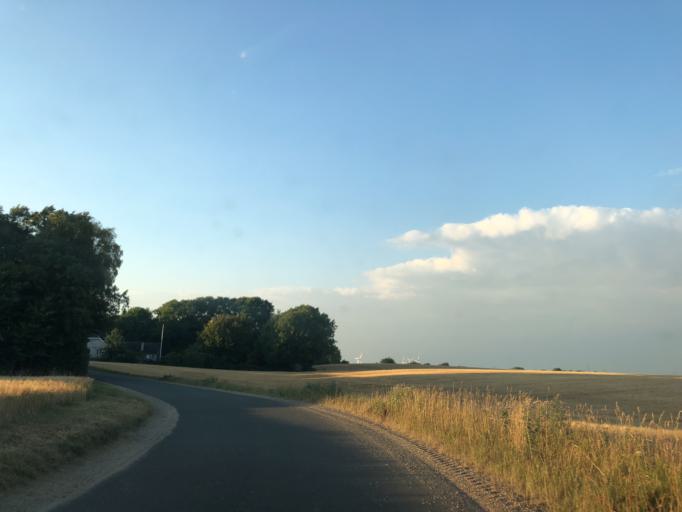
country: DK
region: Central Jutland
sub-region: Holstebro Kommune
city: Holstebro
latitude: 56.3879
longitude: 8.6834
